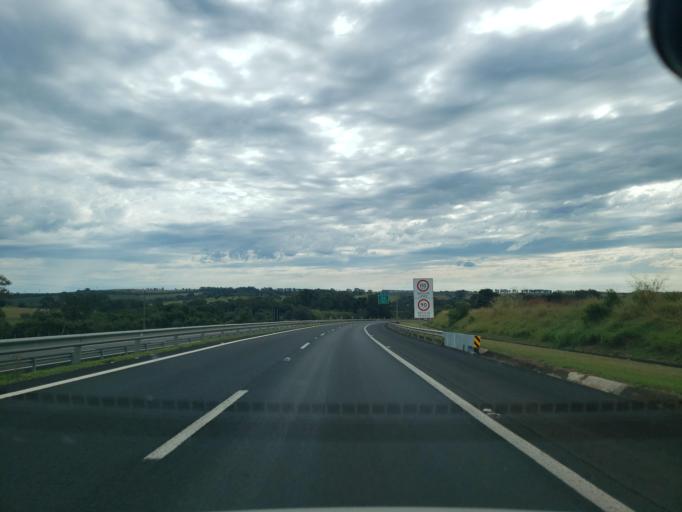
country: BR
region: Sao Paulo
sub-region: Bauru
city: Bauru
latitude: -22.2122
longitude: -49.1777
